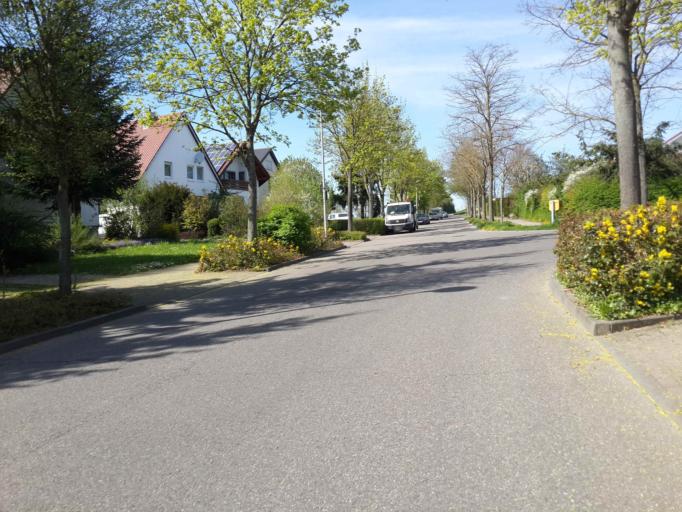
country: DE
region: Baden-Wuerttemberg
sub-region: Regierungsbezirk Stuttgart
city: Neckarsulm
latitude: 49.1708
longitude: 9.1931
